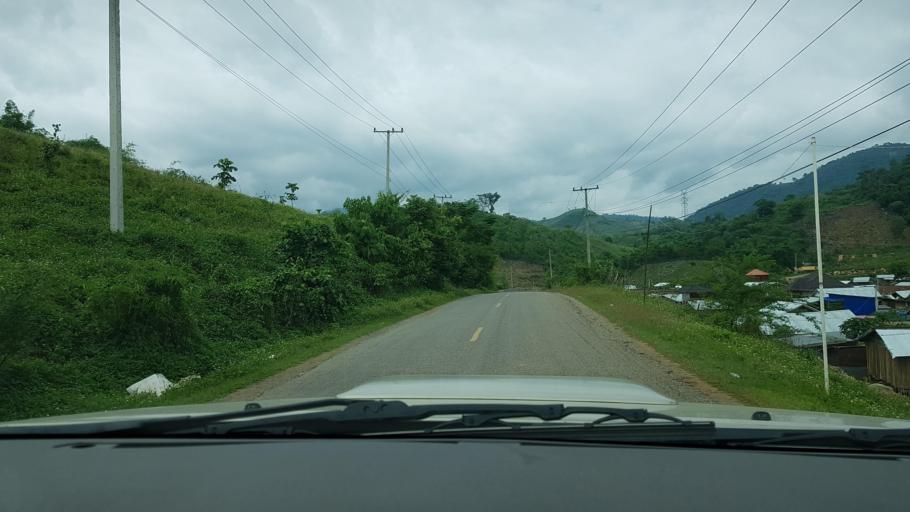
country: TH
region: Nan
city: Chaloem Phra Kiat
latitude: 19.9744
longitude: 101.2687
